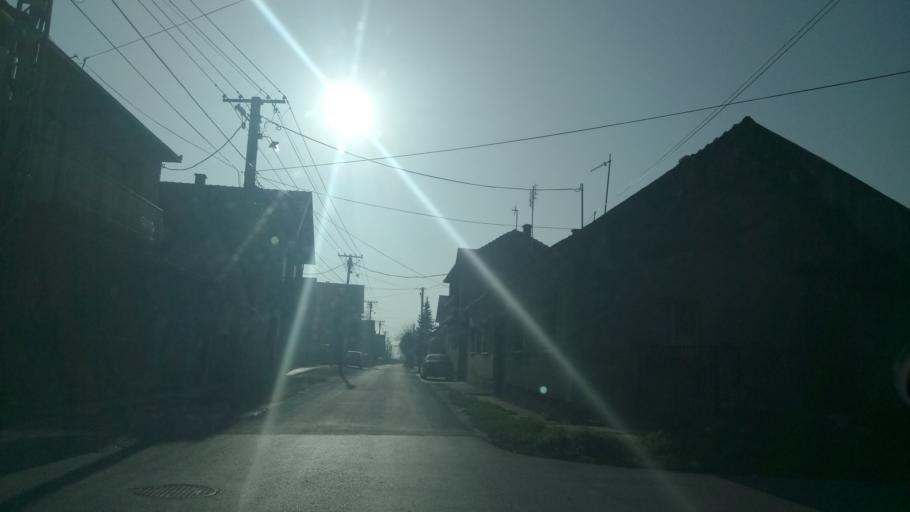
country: RS
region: Autonomna Pokrajina Vojvodina
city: Nova Pazova
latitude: 44.9419
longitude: 20.2067
